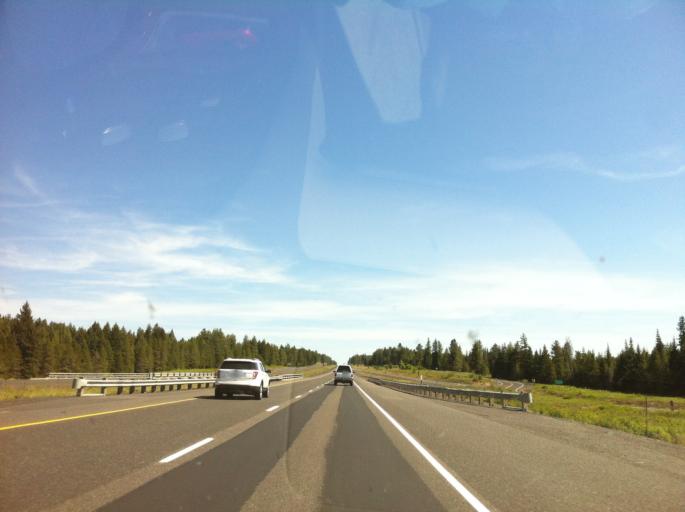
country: US
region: Oregon
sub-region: Umatilla County
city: Mission
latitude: 45.5085
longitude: -118.4281
